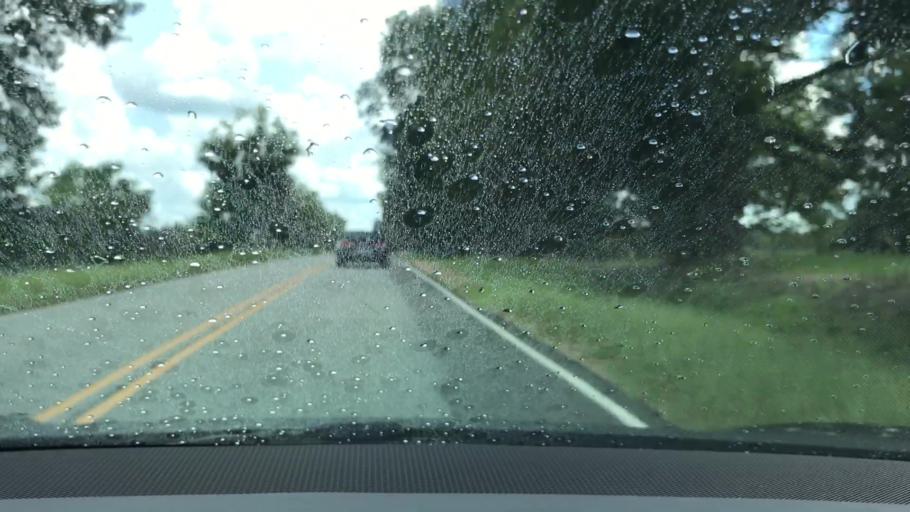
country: US
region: Alabama
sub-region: Montgomery County
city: Pike Road
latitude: 32.2417
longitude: -86.0932
